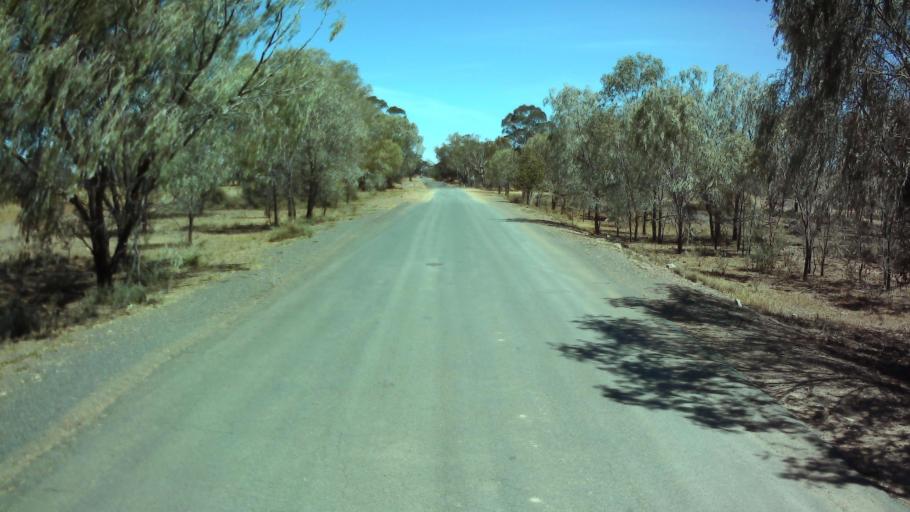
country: AU
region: New South Wales
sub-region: Weddin
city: Grenfell
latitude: -33.8406
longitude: 147.6975
